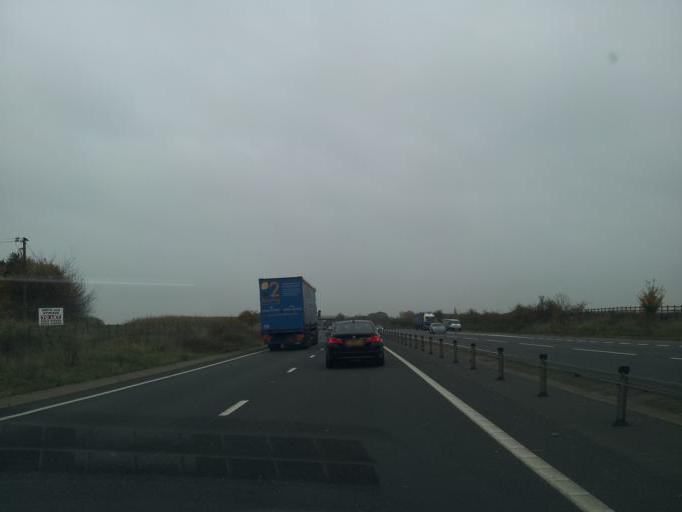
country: GB
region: England
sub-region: Bedford
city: Roxton
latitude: 52.1711
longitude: -0.3345
